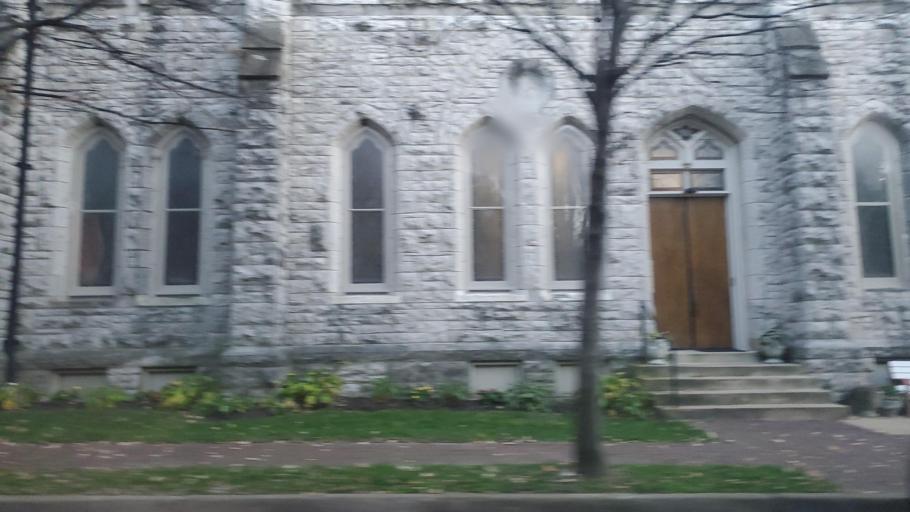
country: US
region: Missouri
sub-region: City of Saint Louis
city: St. Louis
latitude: 38.6168
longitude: -90.2185
